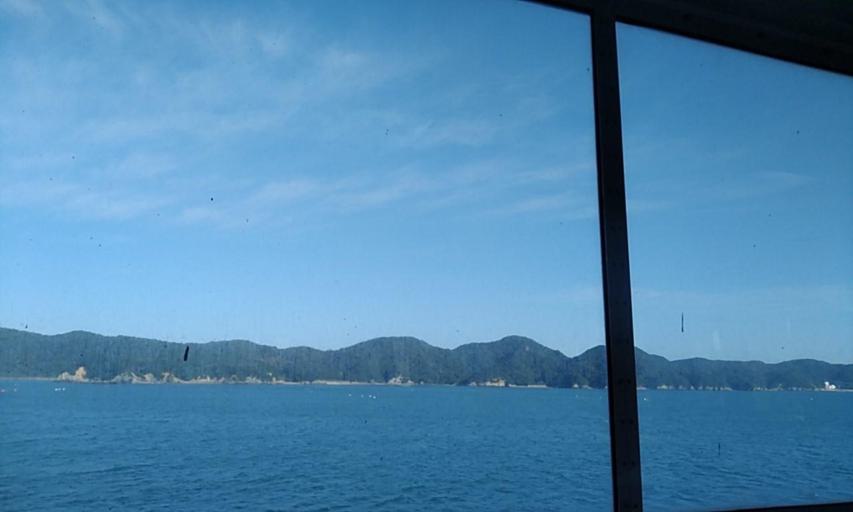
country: JP
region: Mie
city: Toba
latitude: 34.5023
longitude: 136.8802
